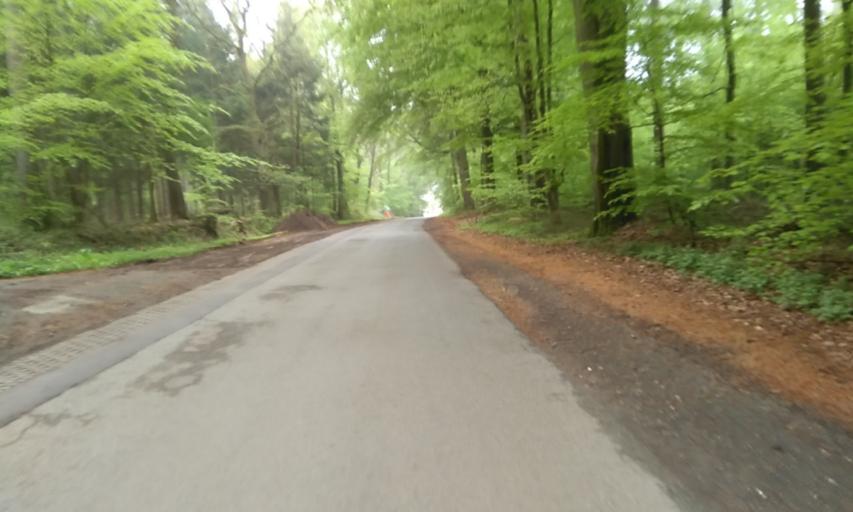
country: DE
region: Lower Saxony
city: Nottensdorf
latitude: 53.4724
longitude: 9.6362
